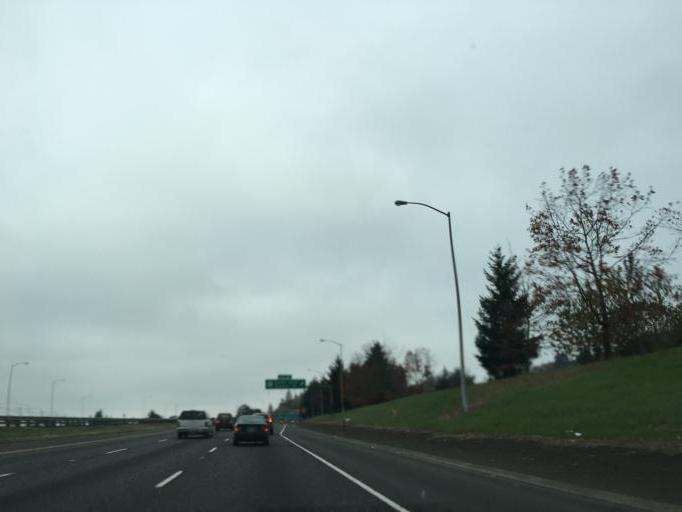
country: US
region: Oregon
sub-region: Multnomah County
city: Lents
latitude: 45.4929
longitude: -122.5654
